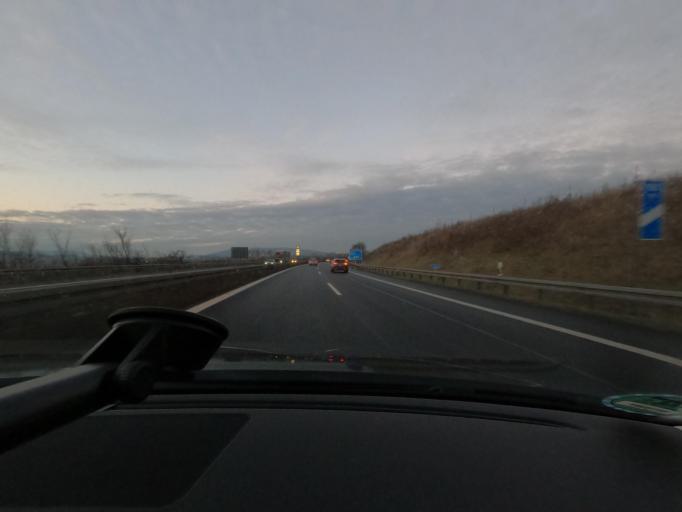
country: DE
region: Bavaria
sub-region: Upper Franconia
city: Breitengussbach
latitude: 49.9685
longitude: 10.8773
